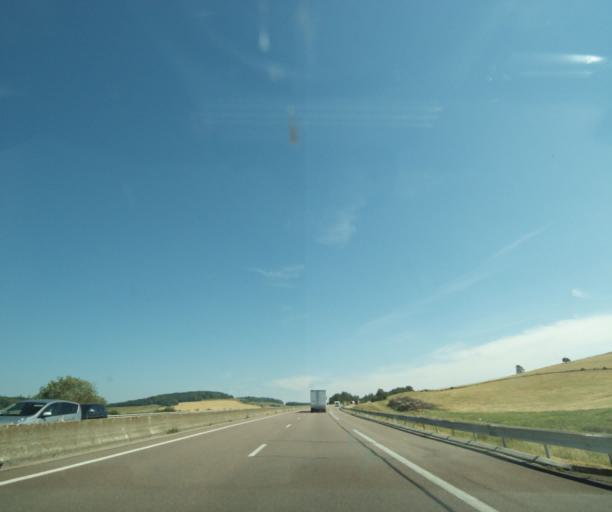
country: FR
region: Lorraine
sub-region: Departement des Vosges
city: Chatenois
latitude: 48.3629
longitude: 5.8670
